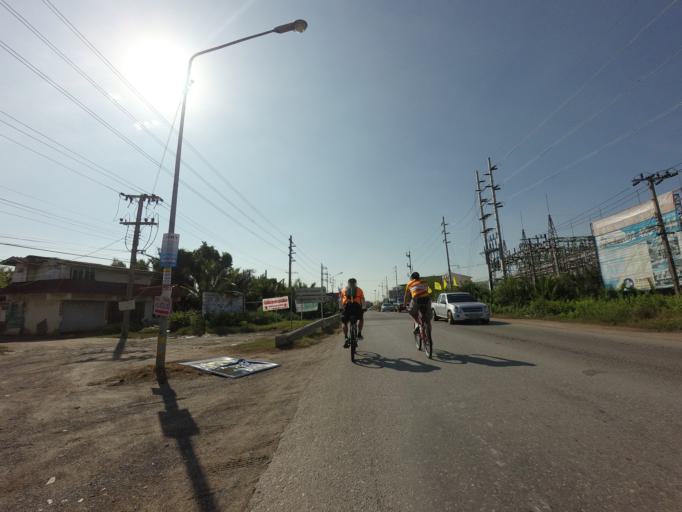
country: TH
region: Samut Prakan
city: Phra Samut Chedi
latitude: 13.5893
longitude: 100.5805
